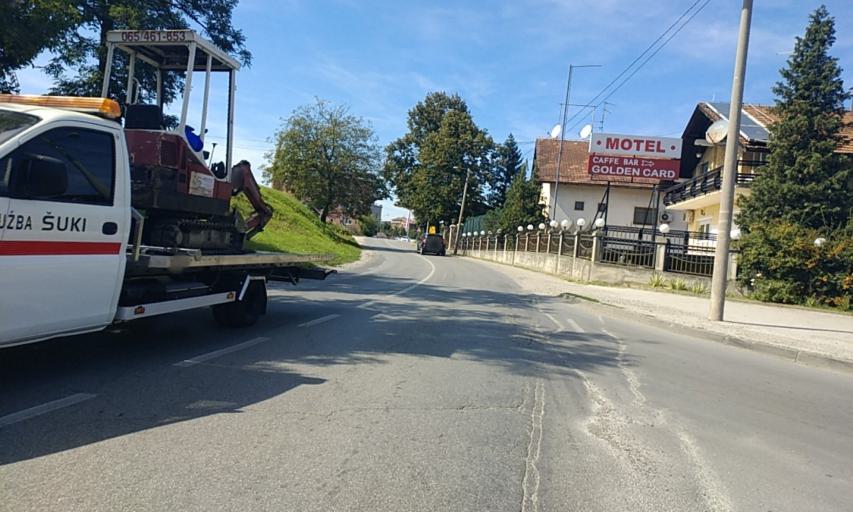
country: BA
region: Republika Srpska
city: Banja Luka
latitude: 44.7897
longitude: 17.2020
